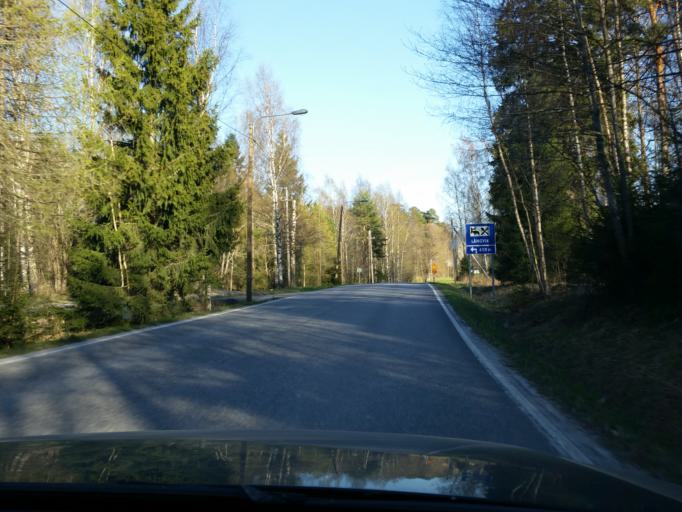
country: FI
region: Uusimaa
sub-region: Helsinki
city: Kirkkonummi
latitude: 60.1119
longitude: 24.5652
